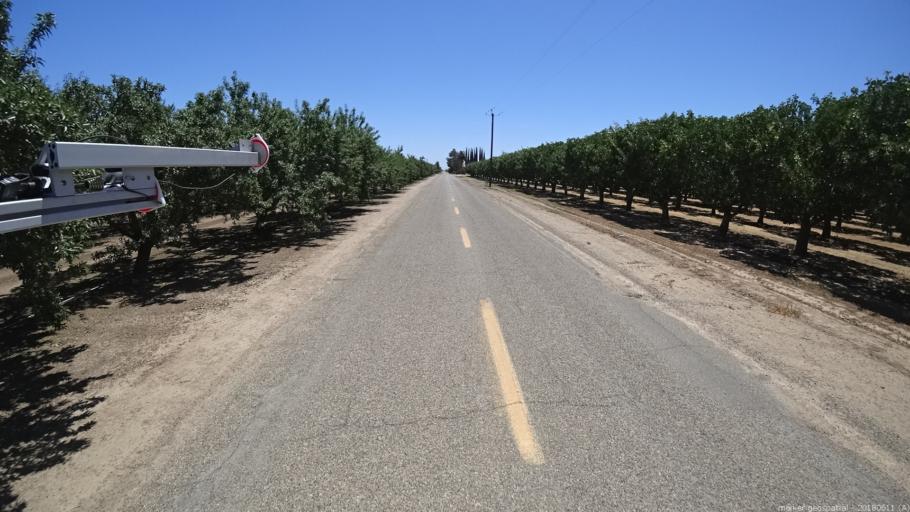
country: US
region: California
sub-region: Madera County
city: Fairmead
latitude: 37.0747
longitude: -120.2114
